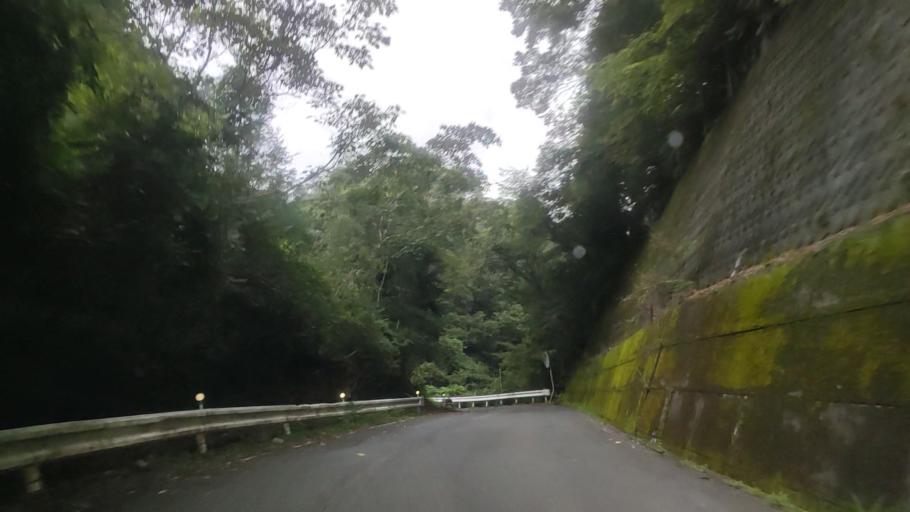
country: JP
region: Wakayama
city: Hashimoto
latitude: 34.2928
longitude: 135.6297
